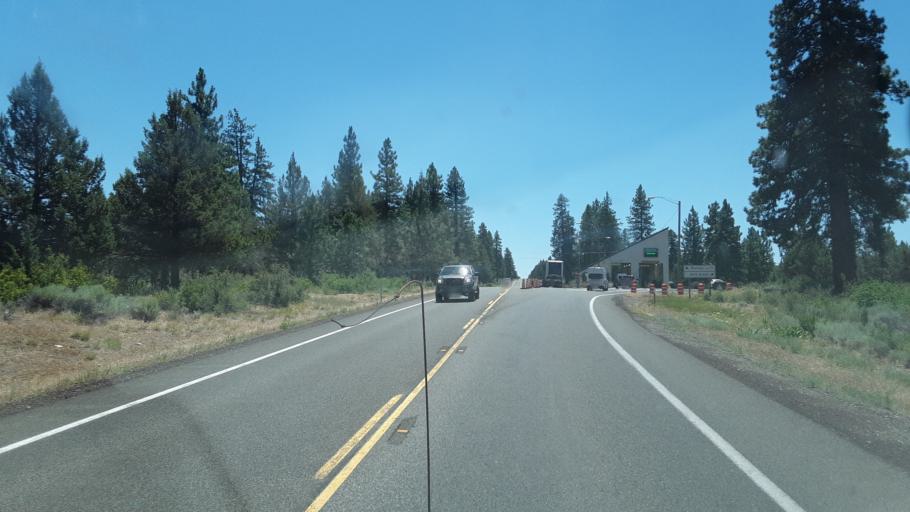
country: US
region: California
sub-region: Siskiyou County
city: Tulelake
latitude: 41.6126
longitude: -121.2134
